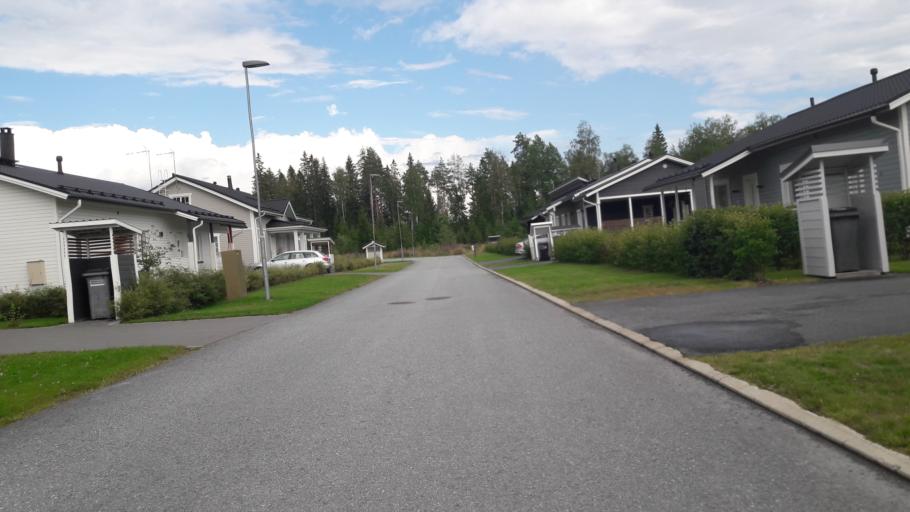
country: FI
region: North Karelia
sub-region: Joensuu
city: Joensuu
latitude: 62.5737
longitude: 29.8277
